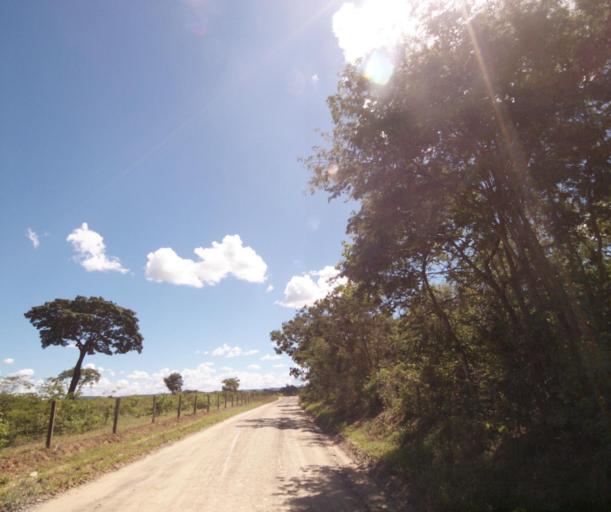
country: BR
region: Bahia
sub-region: Carinhanha
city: Carinhanha
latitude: -14.2269
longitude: -44.3014
